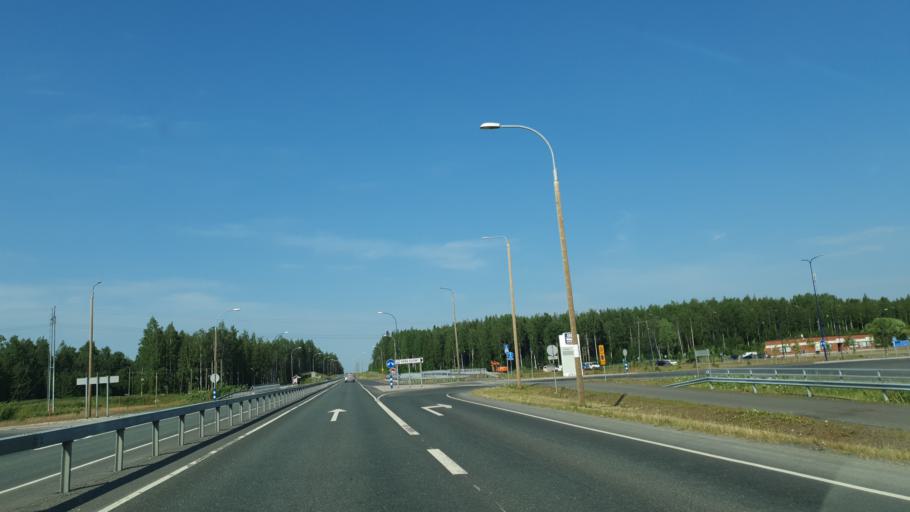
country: FI
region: Northern Savo
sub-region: Kuopio
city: Siilinjaervi
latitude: 63.0991
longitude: 27.7355
